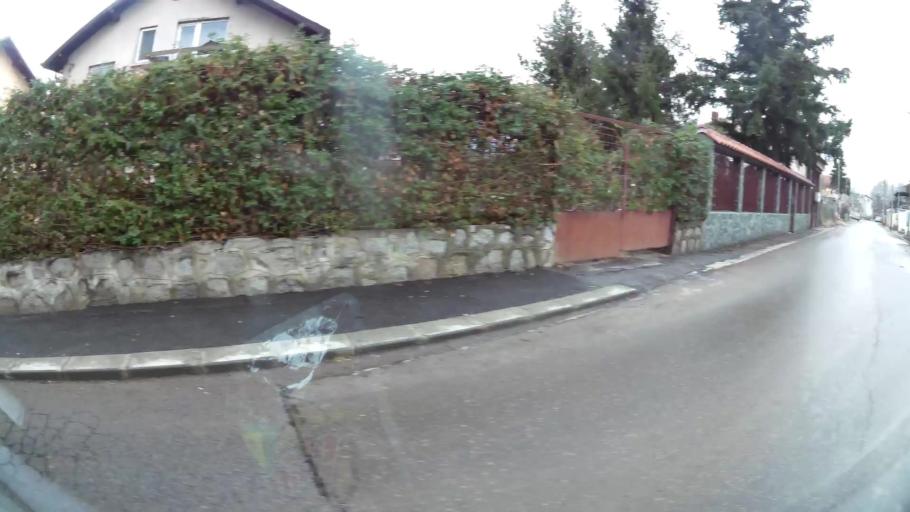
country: BG
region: Sofiya
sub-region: Obshtina Bozhurishte
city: Bozhurishte
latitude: 42.7439
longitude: 23.2678
